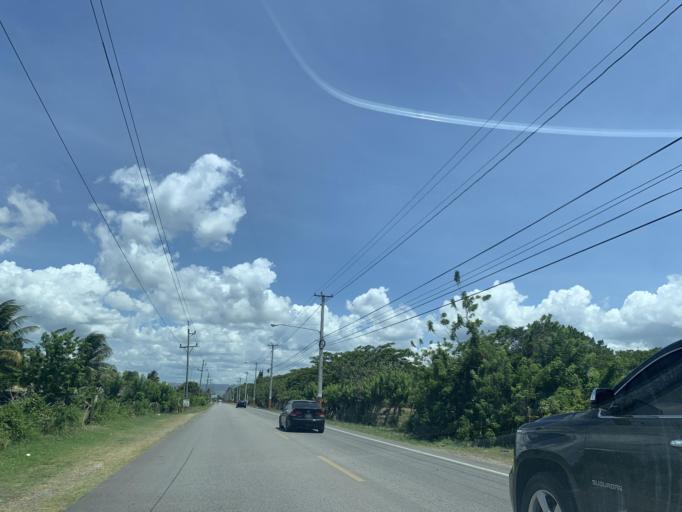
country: DO
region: Puerto Plata
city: Cabarete
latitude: 19.7202
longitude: -70.3865
